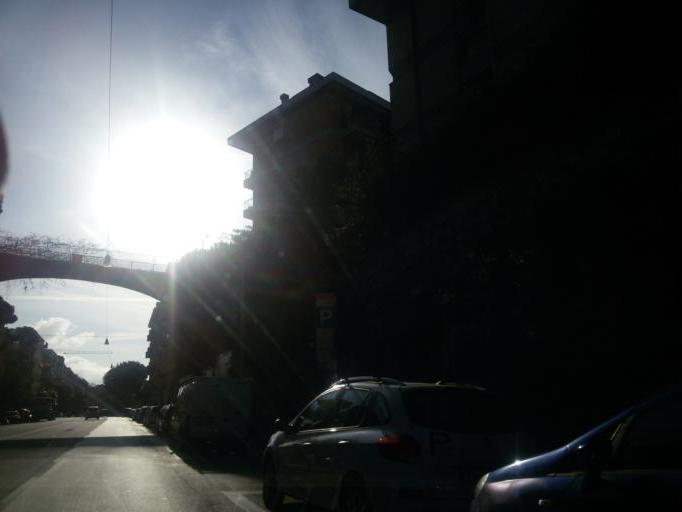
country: IT
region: Liguria
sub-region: Provincia di Genova
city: San Teodoro
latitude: 44.3946
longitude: 8.9639
